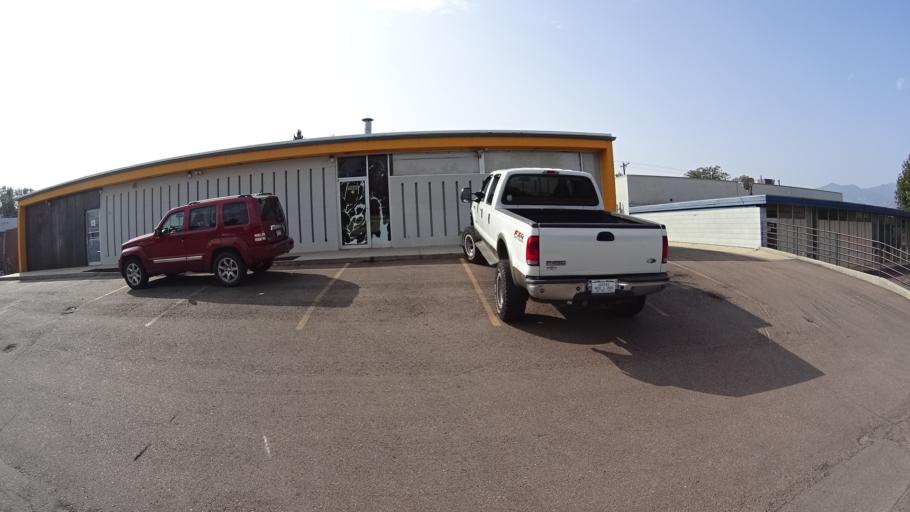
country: US
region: Colorado
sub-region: El Paso County
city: Colorado Springs
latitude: 38.8367
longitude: -104.7789
